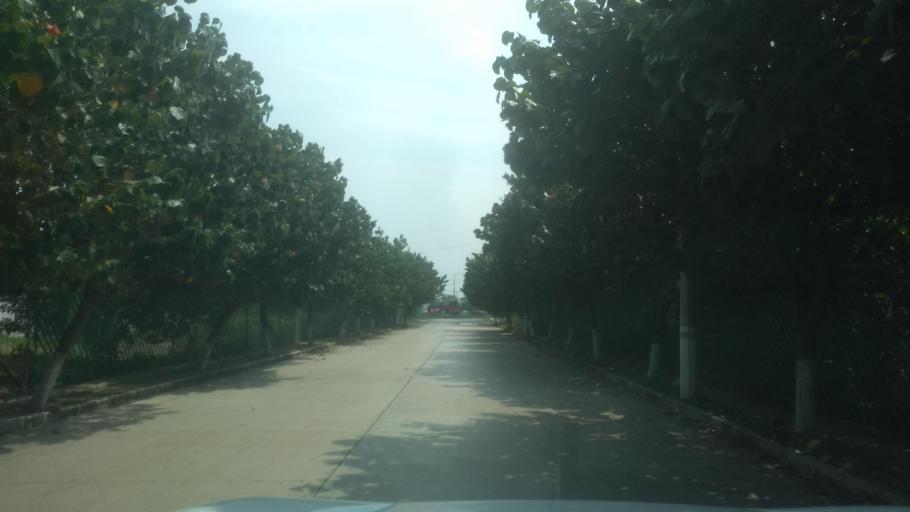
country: MX
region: Veracruz
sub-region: Veracruz
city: Las Amapolas
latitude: 19.1641
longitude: -96.1822
